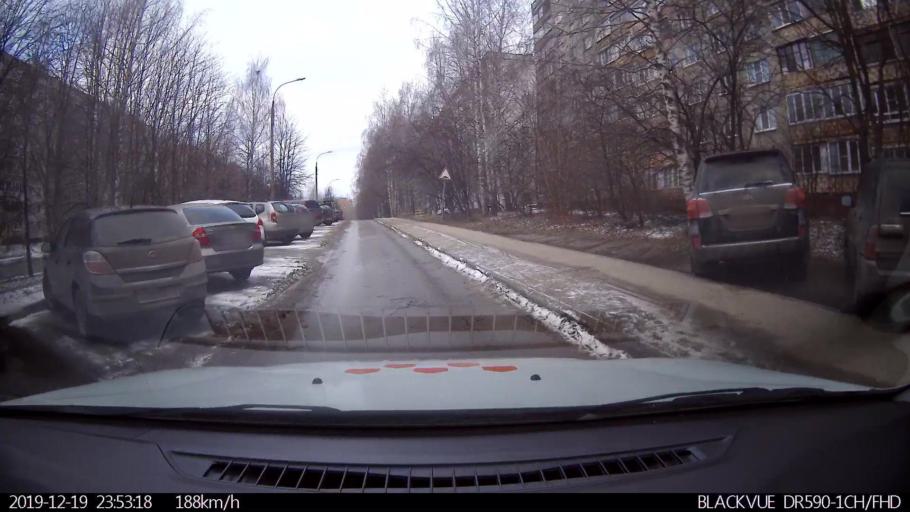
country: RU
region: Vologda
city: Molochnoye
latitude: 58.9634
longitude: 39.4999
